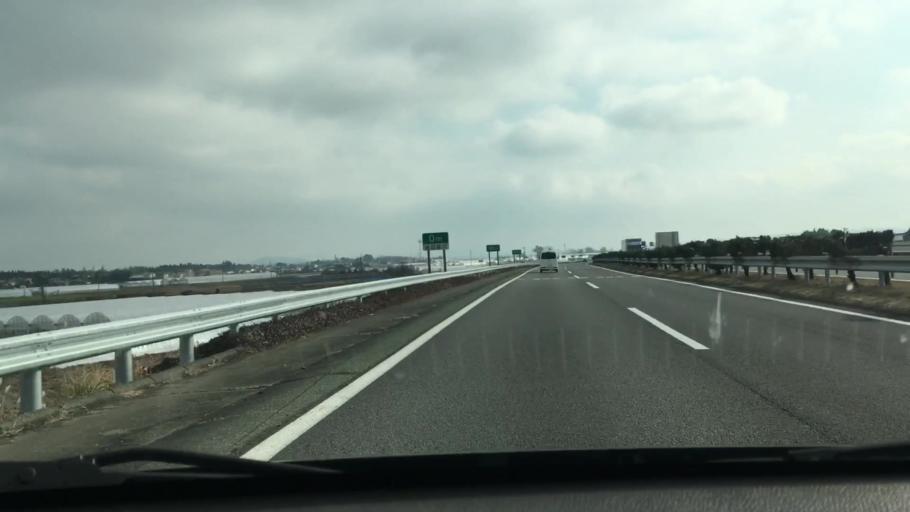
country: JP
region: Kumamoto
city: Ueki
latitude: 32.8876
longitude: 130.7238
